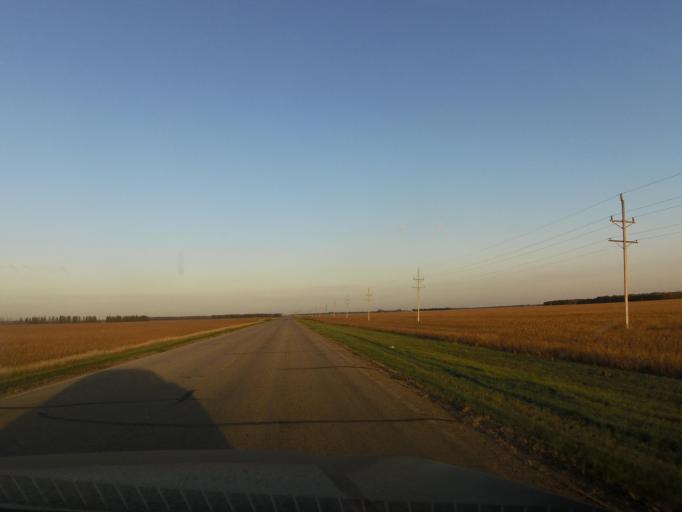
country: CA
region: Manitoba
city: Altona
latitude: 48.9635
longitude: -97.5779
